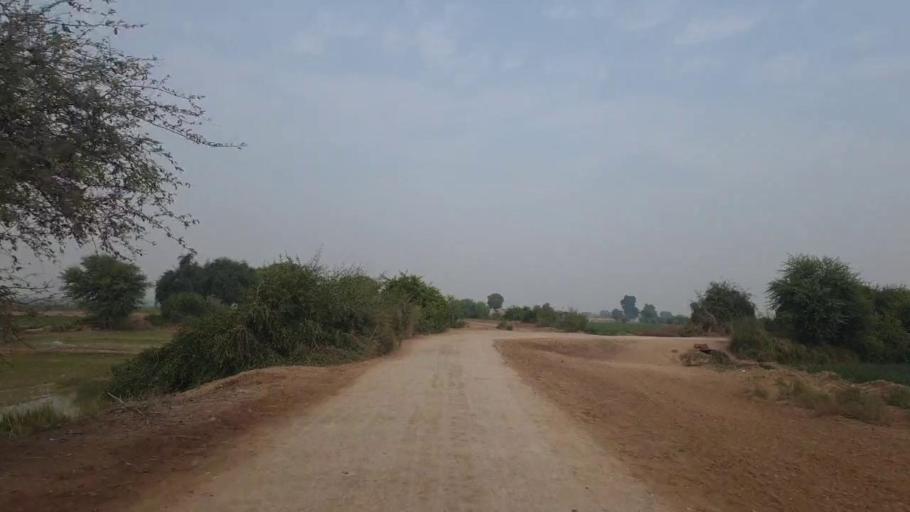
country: PK
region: Sindh
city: Sann
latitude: 25.9936
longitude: 68.1757
